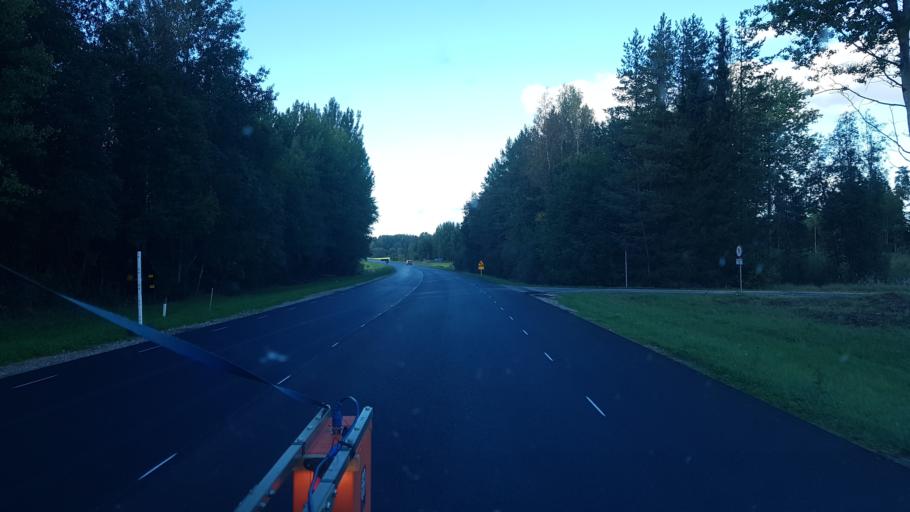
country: EE
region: Valgamaa
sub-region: Valga linn
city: Valga
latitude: 57.8547
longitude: 26.0595
